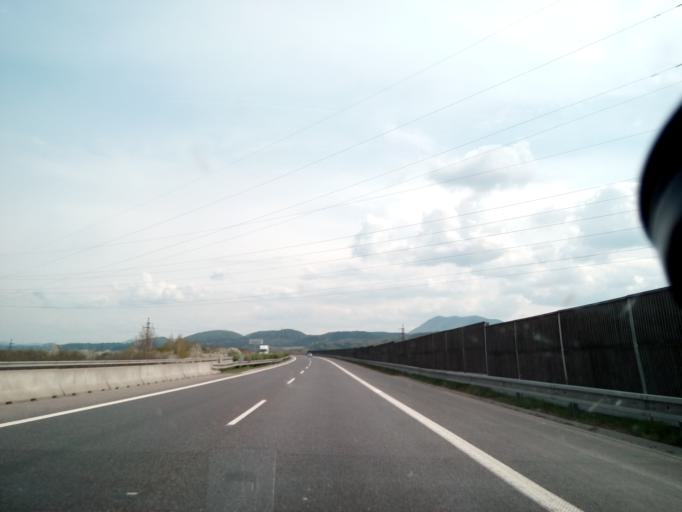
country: SK
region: Nitriansky
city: Ilava
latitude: 49.0459
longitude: 18.2928
